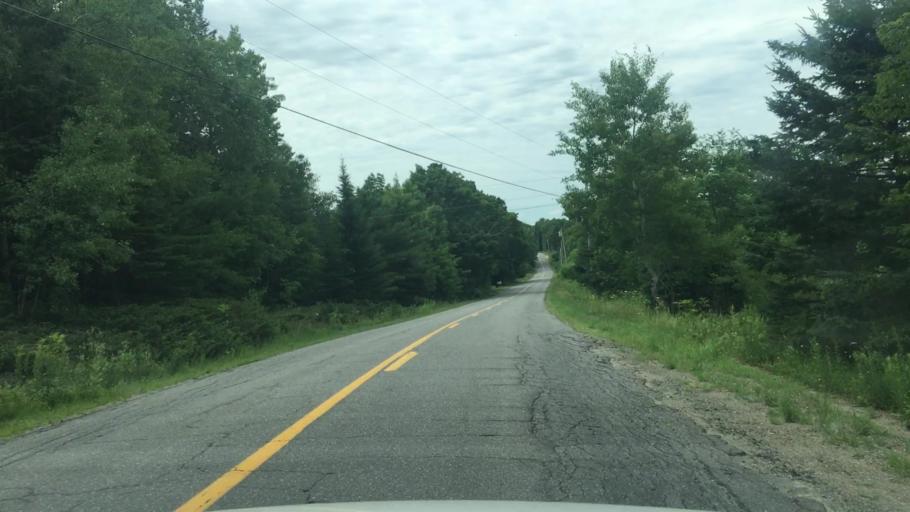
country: US
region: Maine
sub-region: Kennebec County
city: Albion
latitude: 44.4959
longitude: -69.3705
